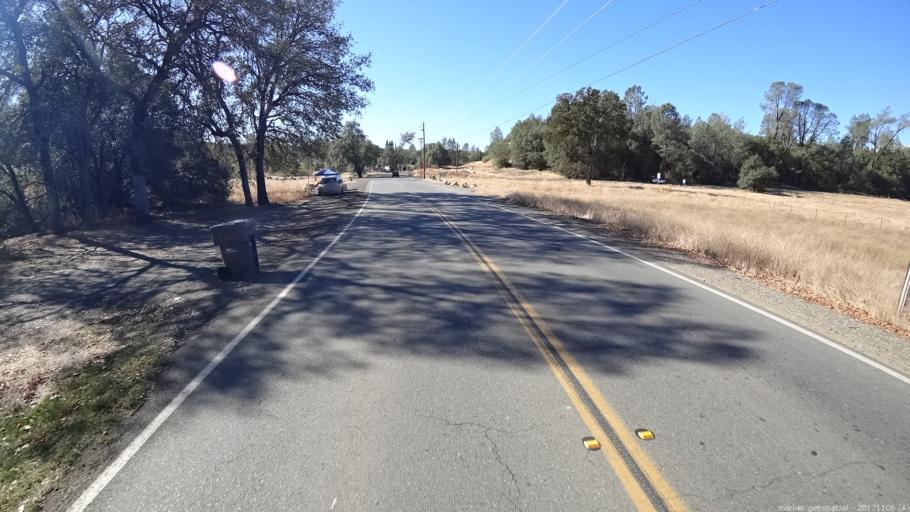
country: US
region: California
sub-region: Shasta County
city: Palo Cedro
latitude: 40.5888
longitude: -122.3057
